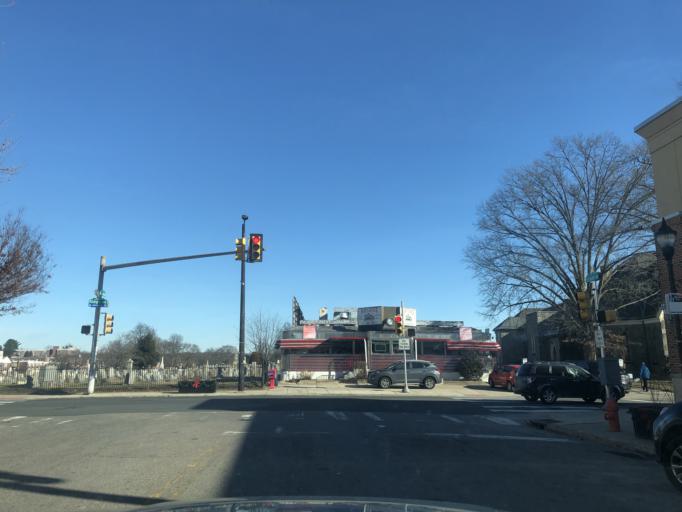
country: US
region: Pennsylvania
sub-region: Montgomery County
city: Bala-Cynwyd
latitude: 40.0327
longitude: -75.2147
